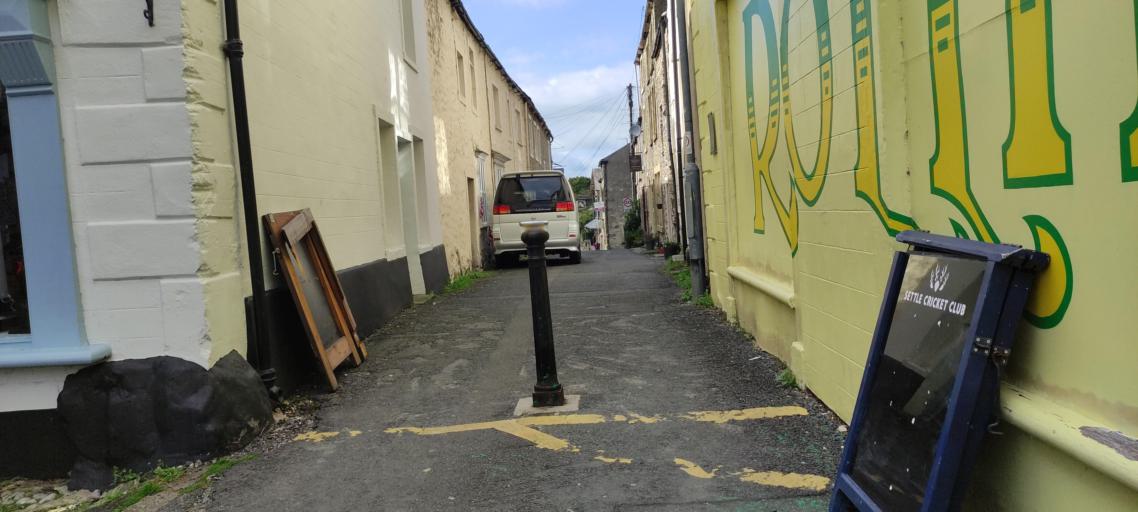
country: GB
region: England
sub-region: North Yorkshire
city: Settle
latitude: 54.0685
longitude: -2.2773
